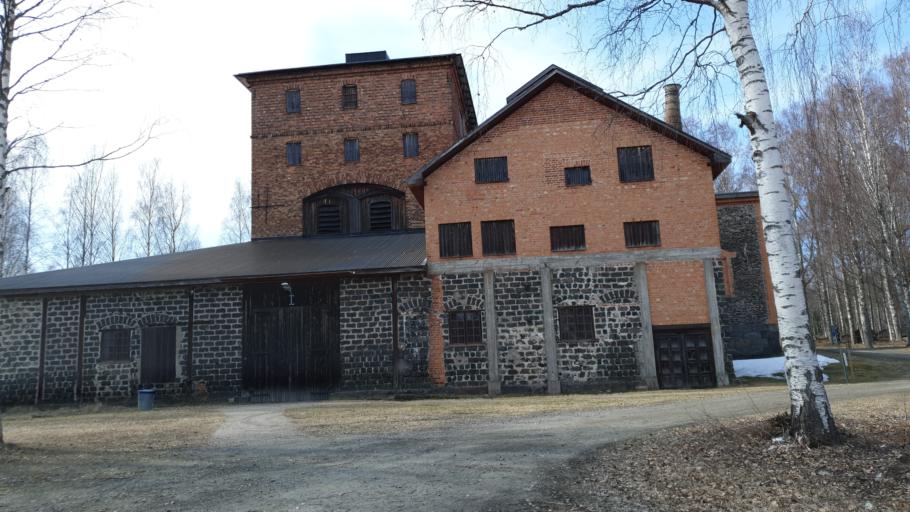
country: SE
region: Gaevleborg
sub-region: Gavle Kommun
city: Norrsundet
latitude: 61.0466
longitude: 17.1504
